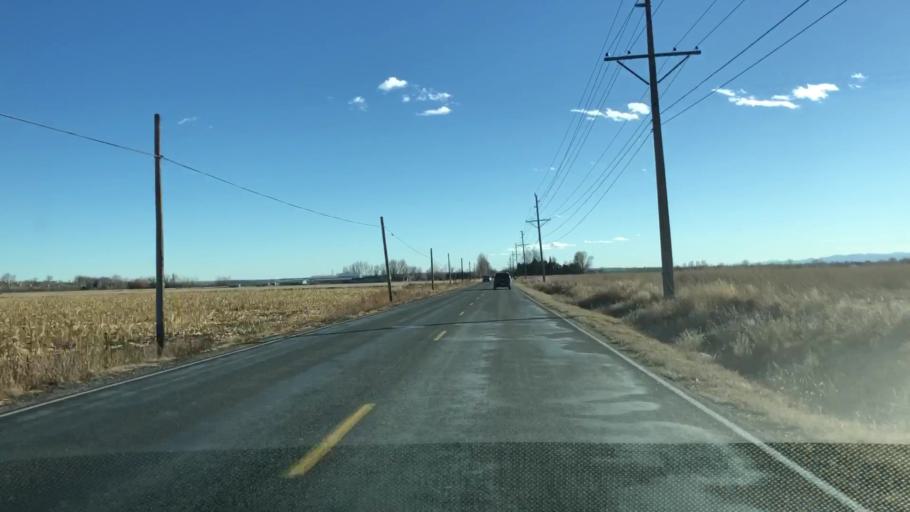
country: US
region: Colorado
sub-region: Larimer County
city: Fort Collins
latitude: 40.5540
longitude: -104.9823
